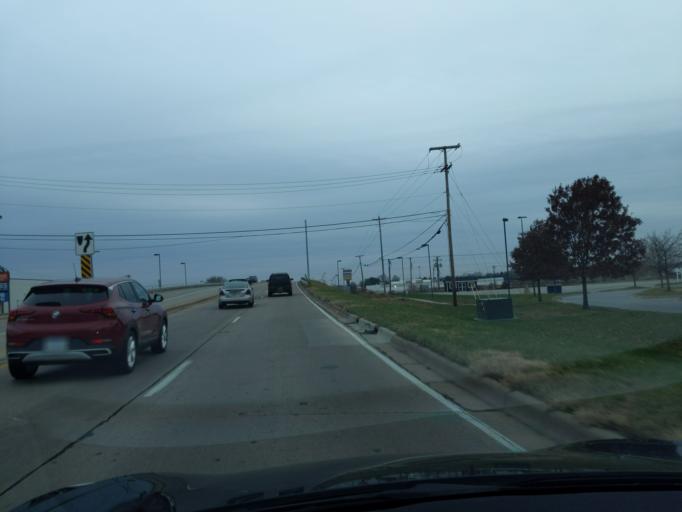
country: US
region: Indiana
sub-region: Saint Joseph County
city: Georgetown
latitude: 41.7181
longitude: -86.1877
